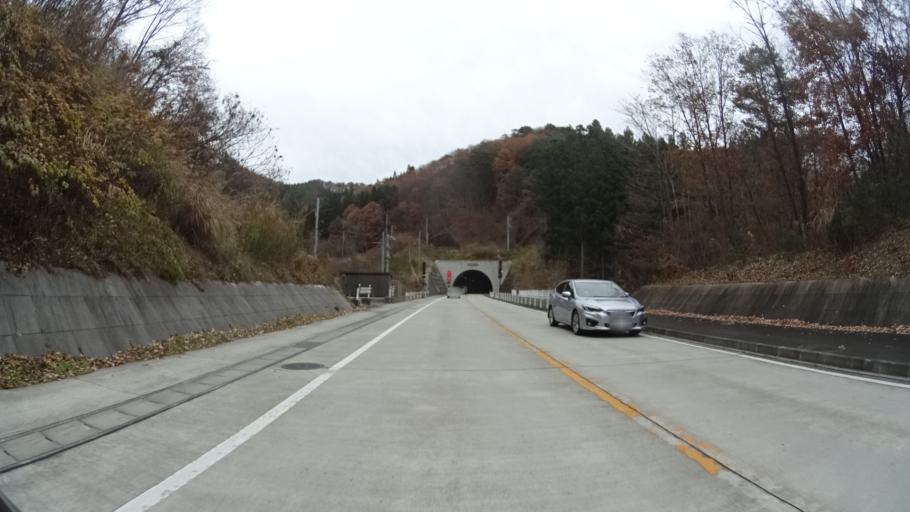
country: JP
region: Gunma
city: Numata
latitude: 36.6653
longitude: 139.1787
